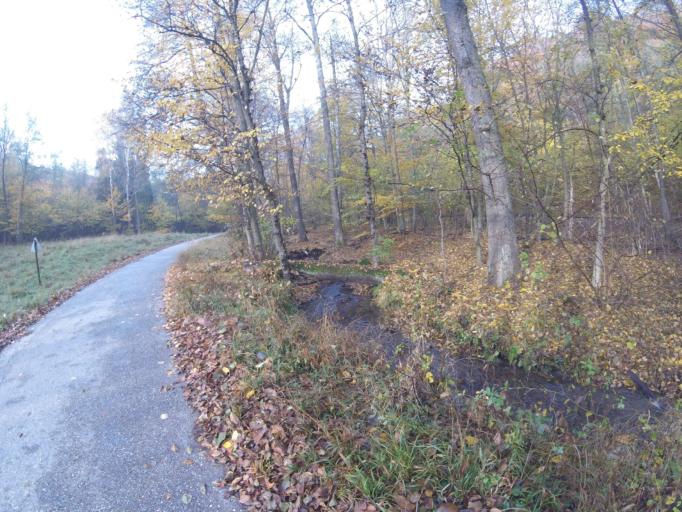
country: HU
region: Borsod-Abauj-Zemplen
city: Tolcsva
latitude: 48.4242
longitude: 21.4311
